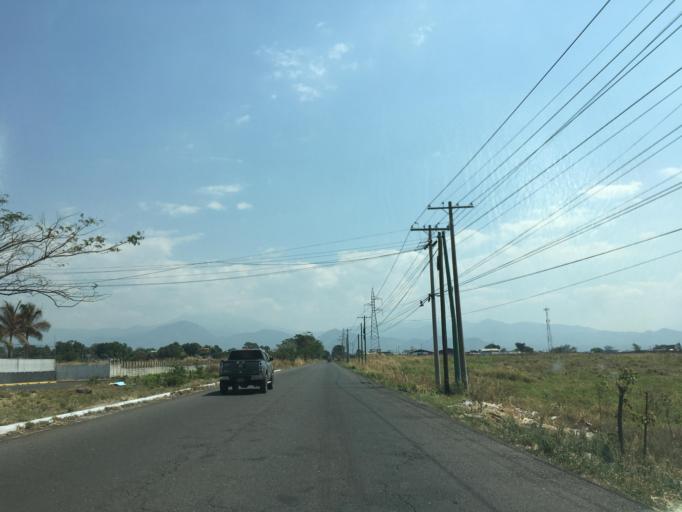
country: GT
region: Escuintla
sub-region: Municipio de Escuintla
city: Escuintla
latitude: 14.2749
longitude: -90.7708
